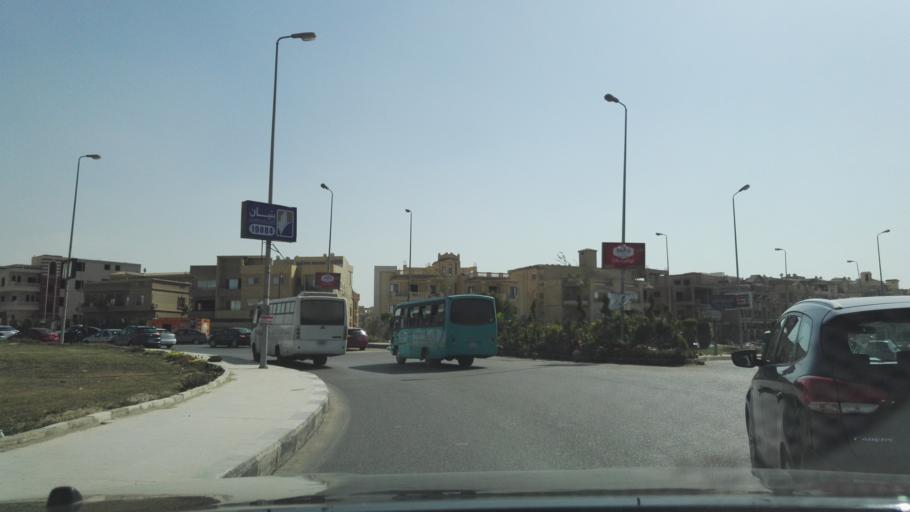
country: EG
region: Muhafazat al Qalyubiyah
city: Al Khankah
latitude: 30.0551
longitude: 31.4745
